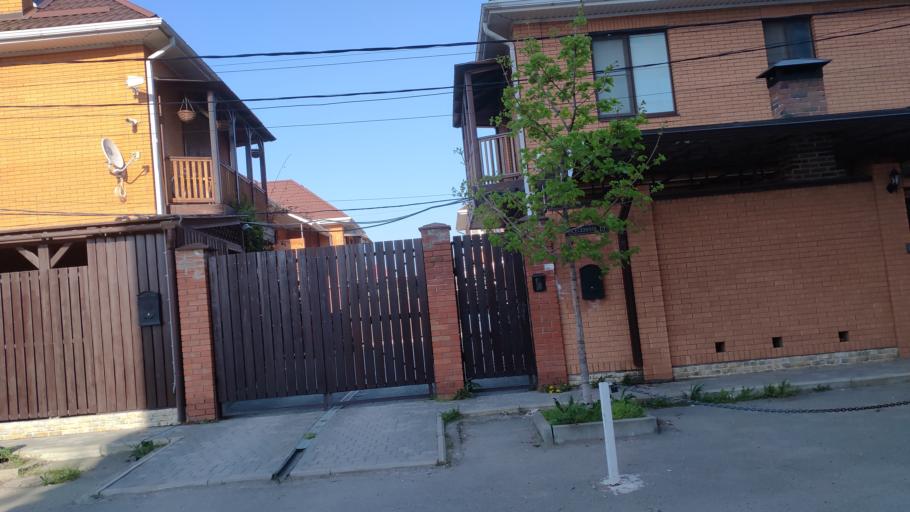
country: RU
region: Krasnodarskiy
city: Krasnodar
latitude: 45.0788
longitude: 39.0107
